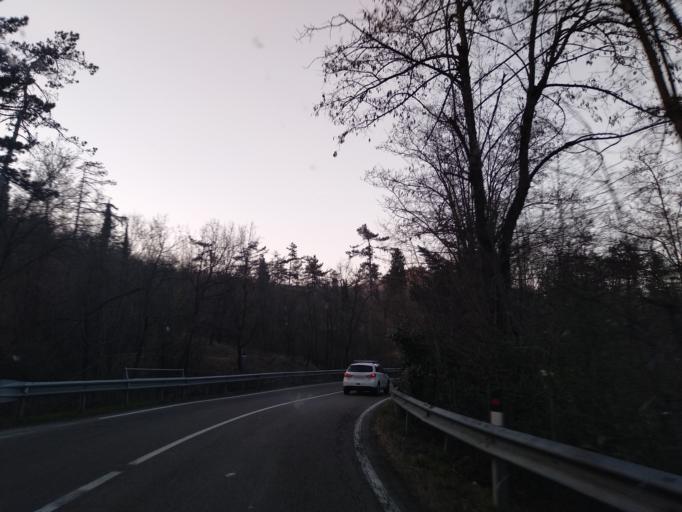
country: IT
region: Emilia-Romagna
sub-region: Provincia di Reggio Emilia
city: Vezzano sul Crostolo
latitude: 44.5855
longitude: 10.5343
